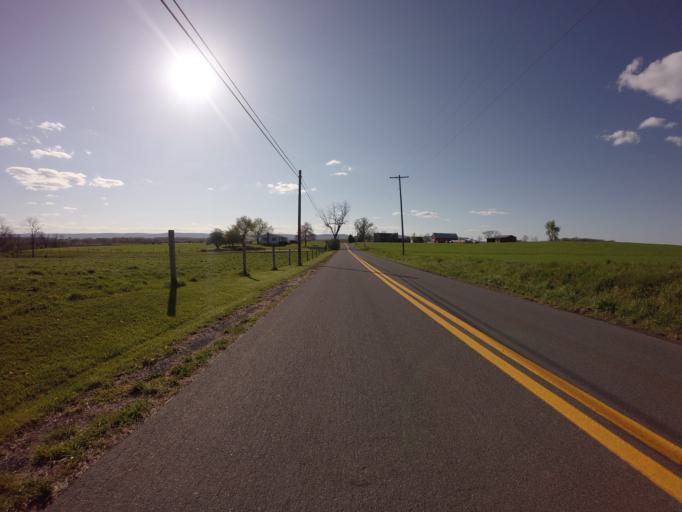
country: US
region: Maryland
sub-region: Frederick County
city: Woodsboro
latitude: 39.6199
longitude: -77.2776
